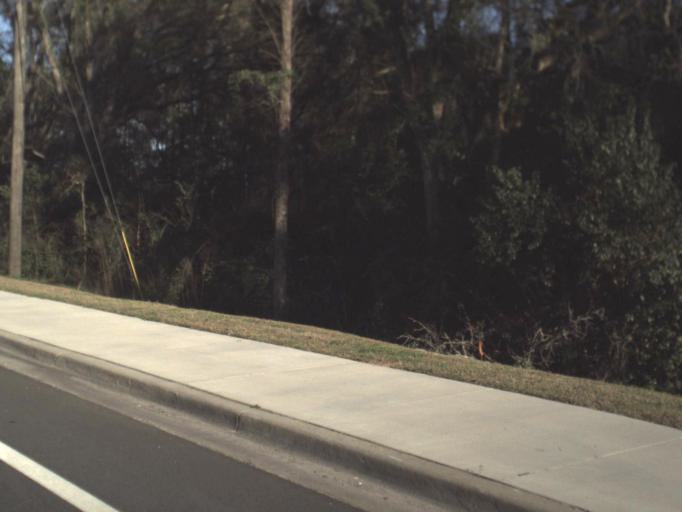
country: US
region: Florida
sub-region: Leon County
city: Tallahassee
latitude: 30.4811
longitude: -84.1694
